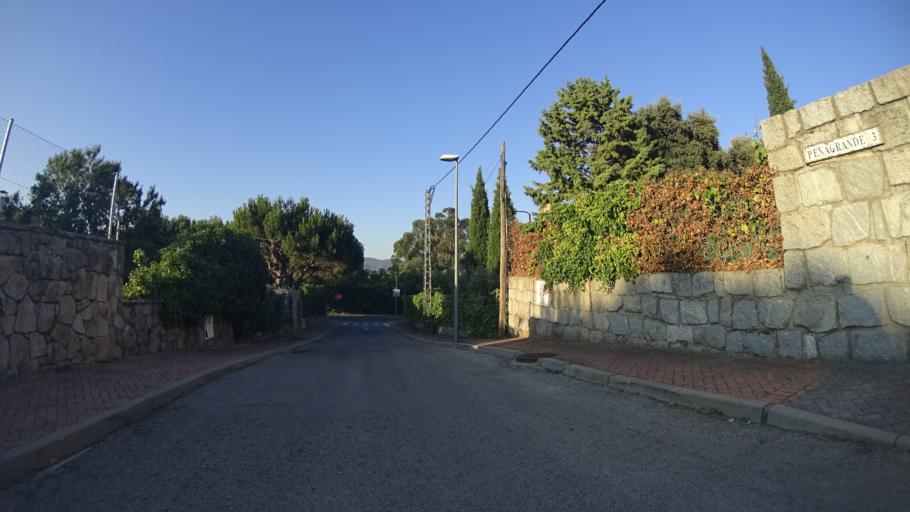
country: ES
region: Madrid
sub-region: Provincia de Madrid
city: Galapagar
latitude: 40.5701
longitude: -3.9990
